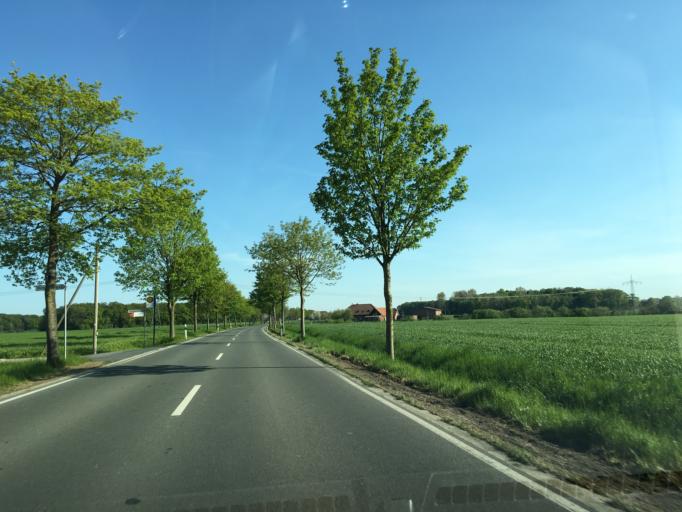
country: DE
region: North Rhine-Westphalia
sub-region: Regierungsbezirk Munster
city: Senden
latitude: 51.7993
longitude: 7.5373
